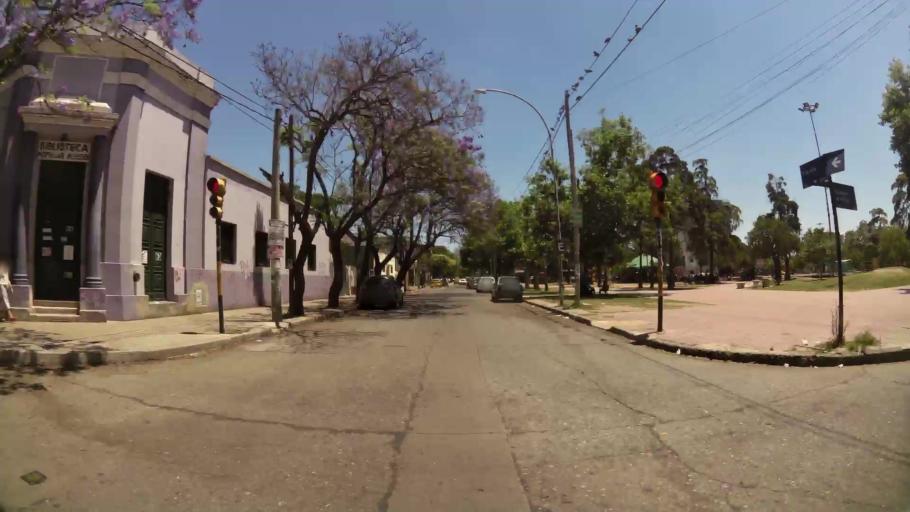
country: AR
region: Cordoba
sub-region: Departamento de Capital
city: Cordoba
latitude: -31.4045
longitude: -64.2176
